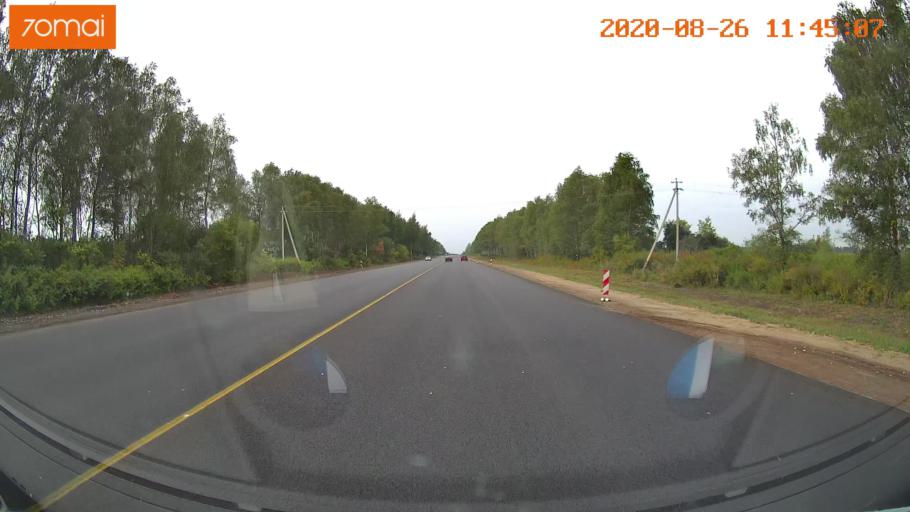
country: RU
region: Rjazan
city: Lesnoy
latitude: 54.2972
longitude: 40.6383
